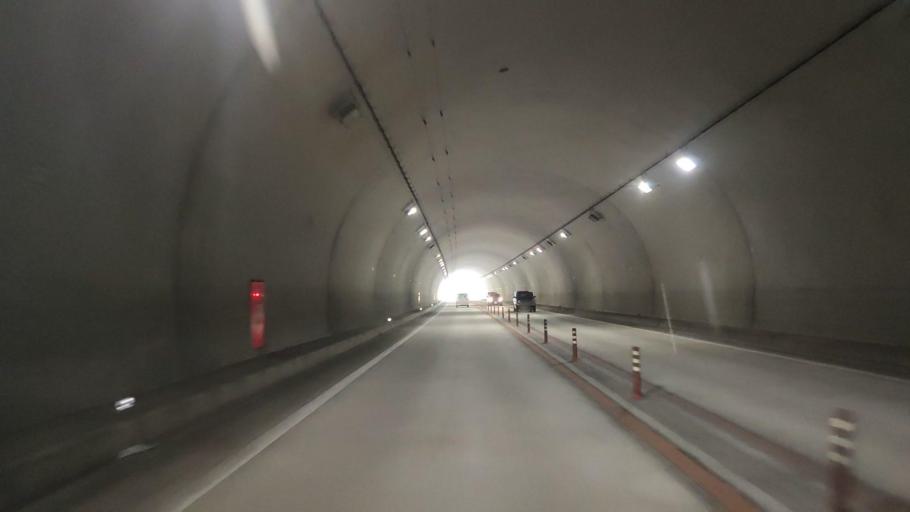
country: JP
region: Wakayama
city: Shingu
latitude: 33.6149
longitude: 135.9171
